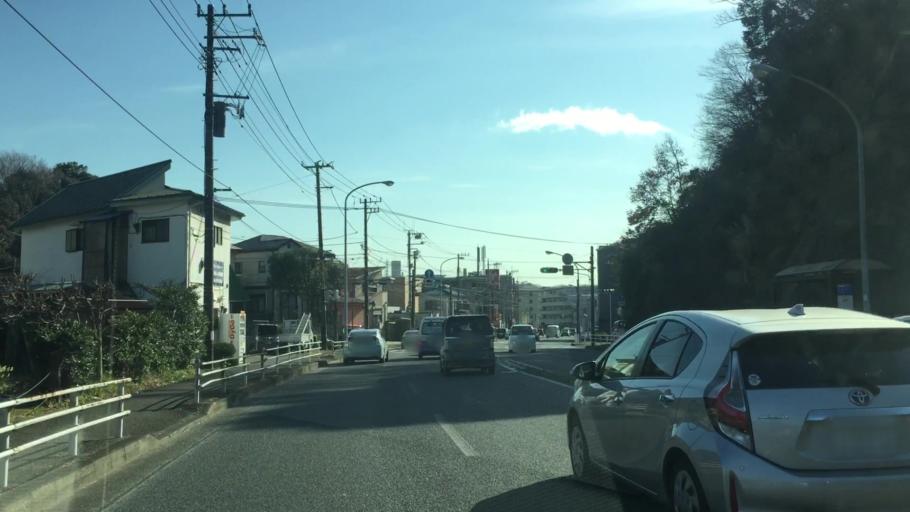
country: JP
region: Kanagawa
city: Zushi
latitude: 35.3497
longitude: 139.6077
